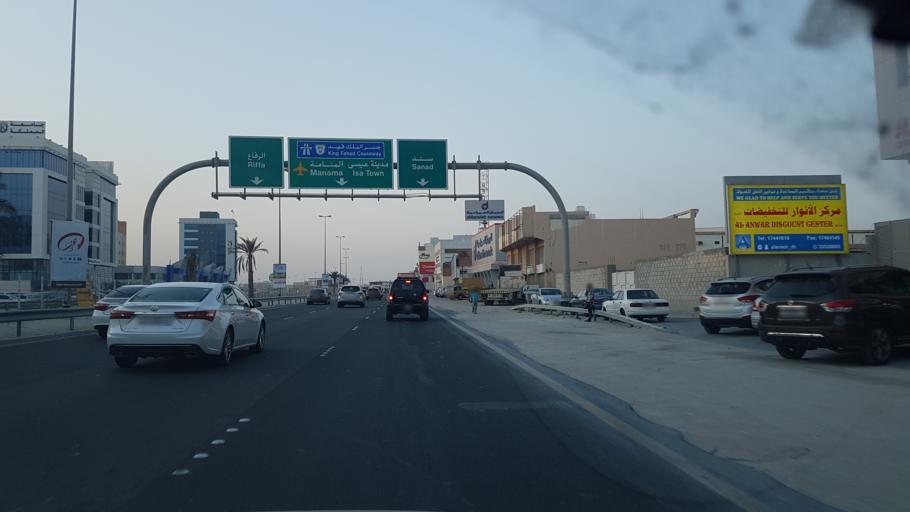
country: BH
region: Northern
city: Ar Rifa'
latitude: 26.1351
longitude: 50.5846
